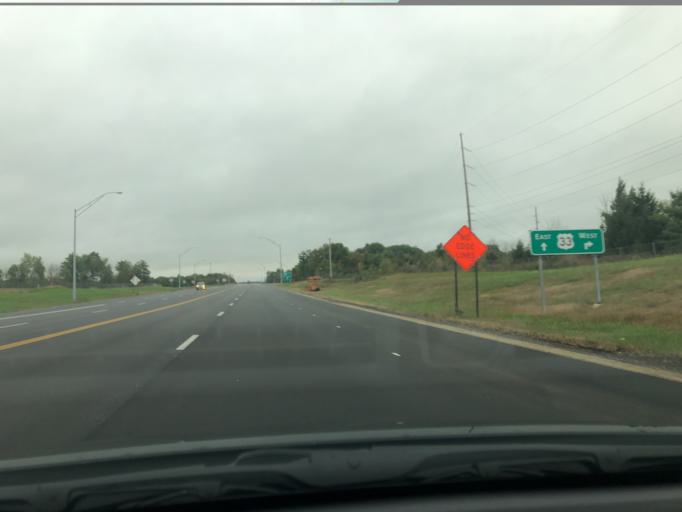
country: US
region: Ohio
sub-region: Champaign County
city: North Lewisburg
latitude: 40.3263
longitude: -83.5817
